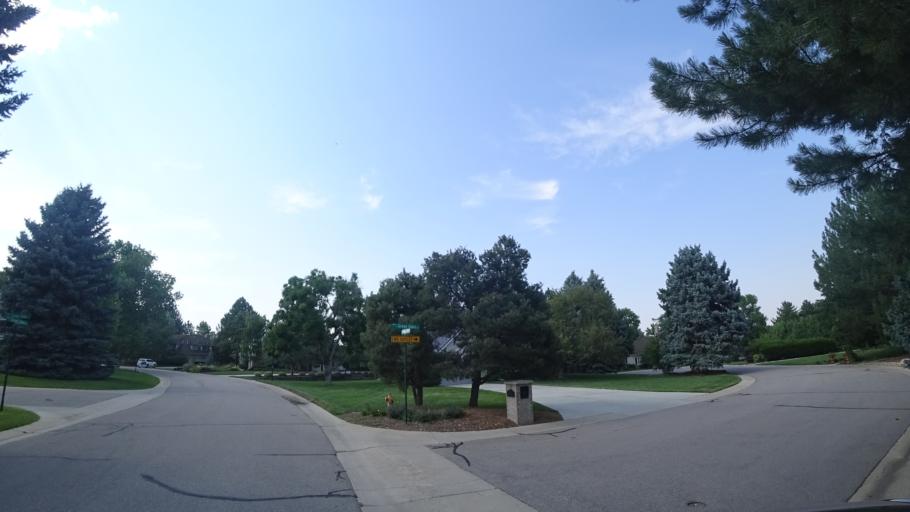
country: US
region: Colorado
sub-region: Arapahoe County
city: Greenwood Village
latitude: 39.6123
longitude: -104.9612
